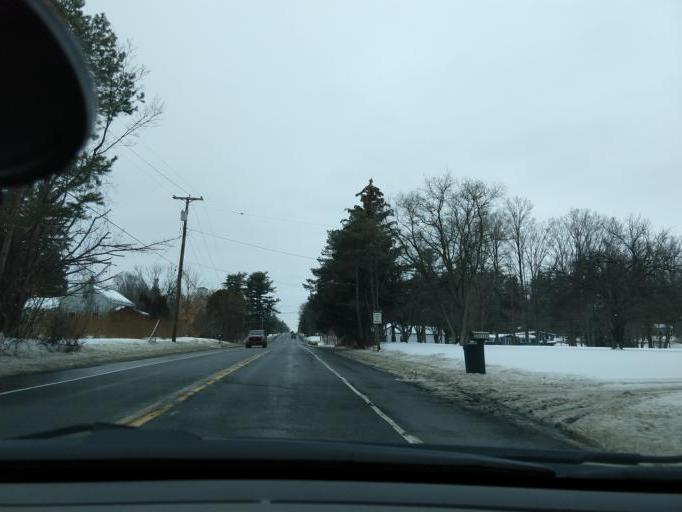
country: US
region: New York
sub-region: Tompkins County
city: Lansing
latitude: 42.5254
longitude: -76.4917
